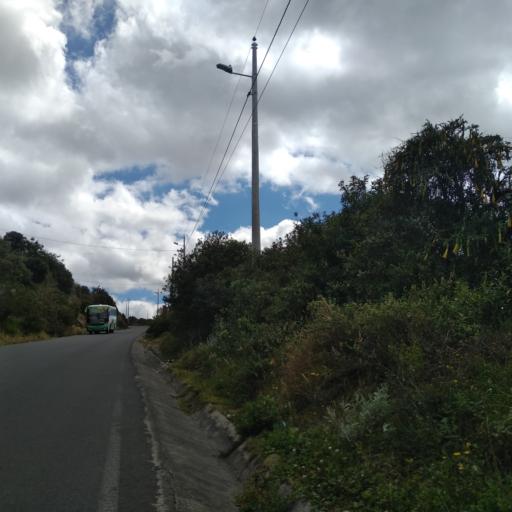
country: EC
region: Cotopaxi
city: Saquisili
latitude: -0.7521
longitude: -78.7288
